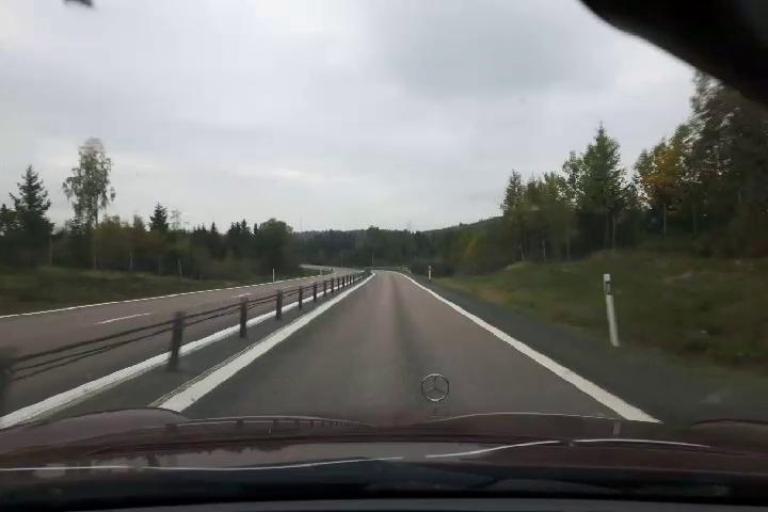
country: SE
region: Vaesternorrland
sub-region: Kramfors Kommun
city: Nordingra
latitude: 62.9112
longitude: 18.0930
